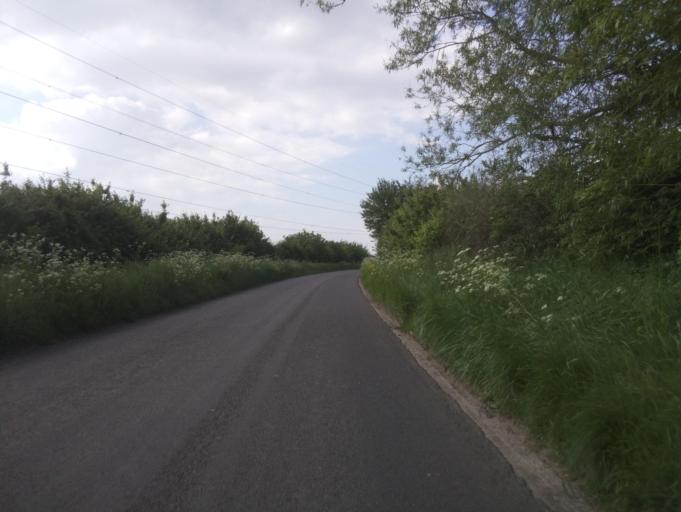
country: GB
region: England
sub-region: Wiltshire
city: Bremhill
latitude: 51.4977
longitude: -2.0739
